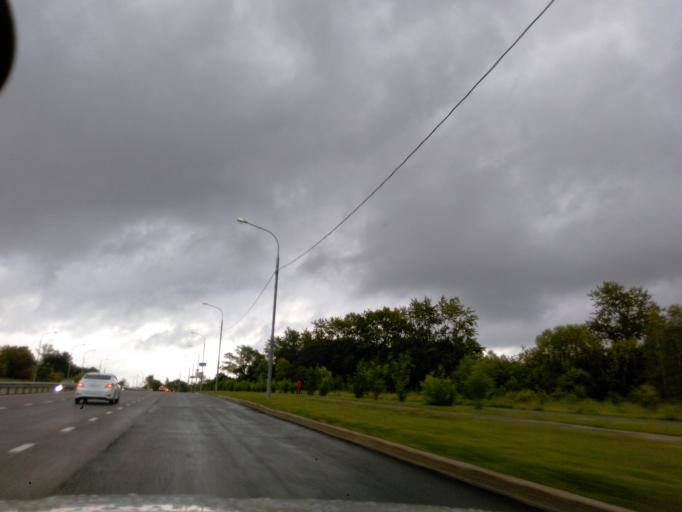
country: RU
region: Moscow
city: Zelenograd
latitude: 55.9701
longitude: 37.1790
